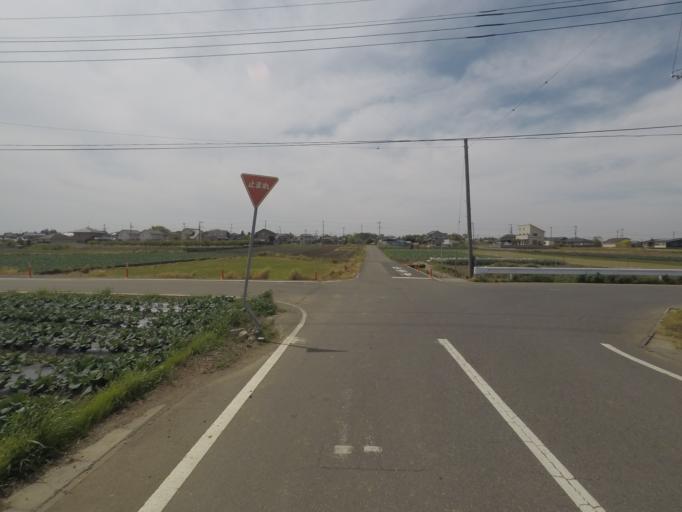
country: JP
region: Ibaraki
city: Ishige
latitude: 36.1005
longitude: 140.0170
